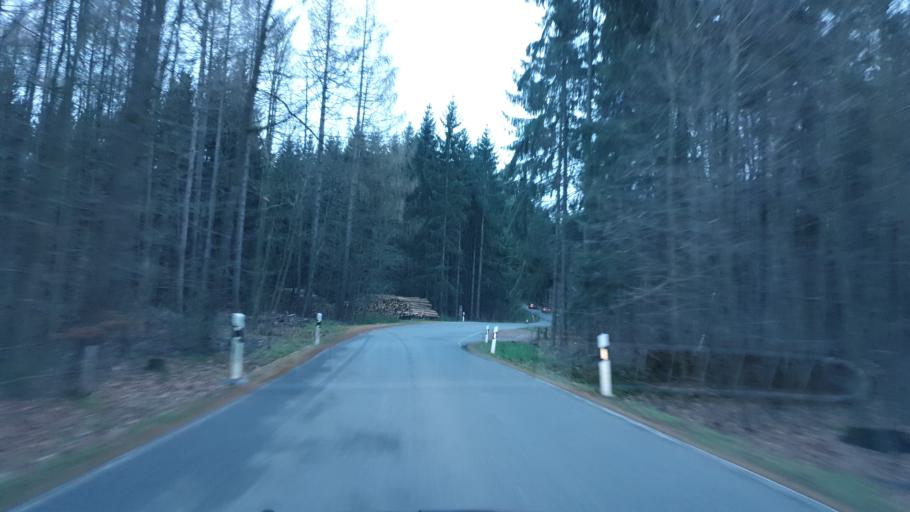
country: DE
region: Saxony
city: Hartenstein
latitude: 50.6447
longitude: 12.6537
